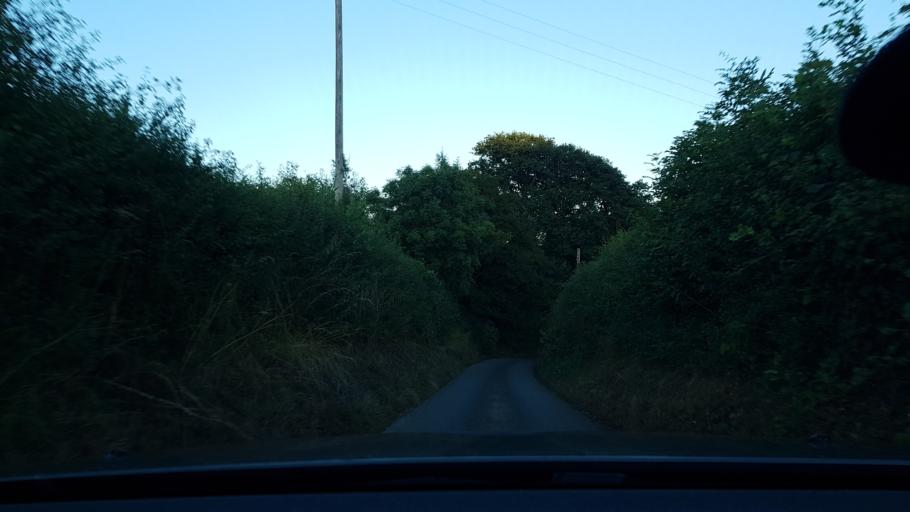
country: GB
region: England
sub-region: Wiltshire
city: Shalbourne
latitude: 51.3857
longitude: -1.5392
